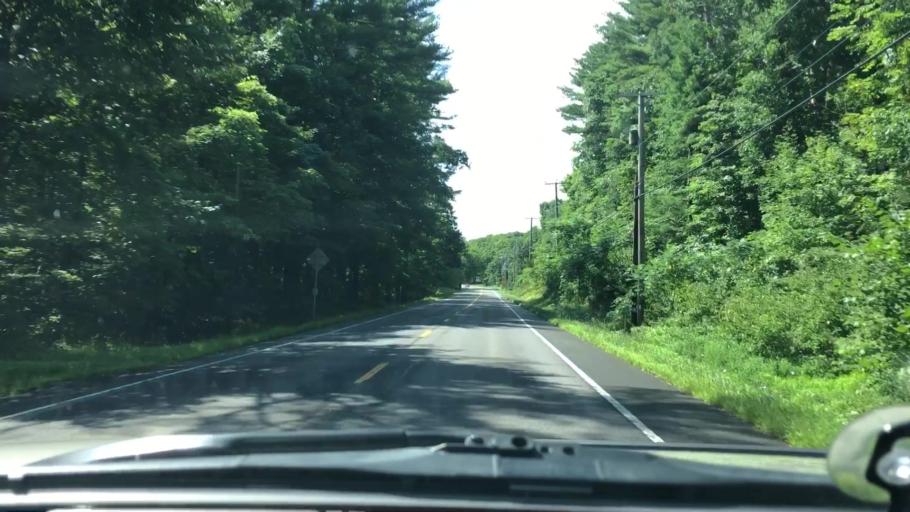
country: US
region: New York
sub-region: Greene County
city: Cairo
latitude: 42.2580
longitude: -73.9773
